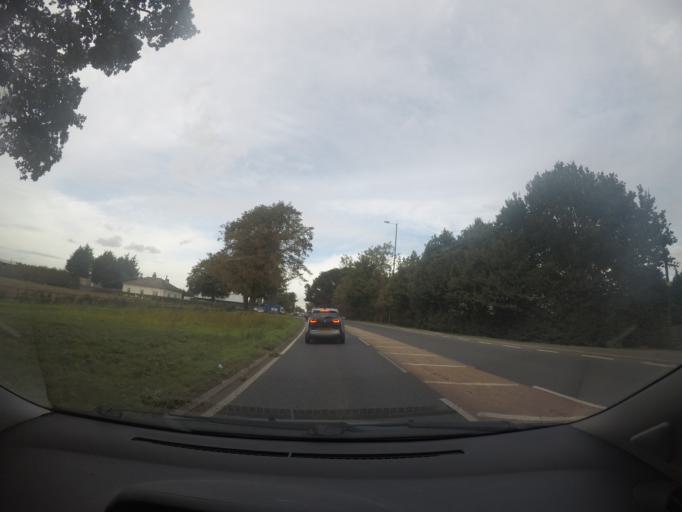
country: GB
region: England
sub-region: City of York
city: Deighton
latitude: 53.9134
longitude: -1.0512
